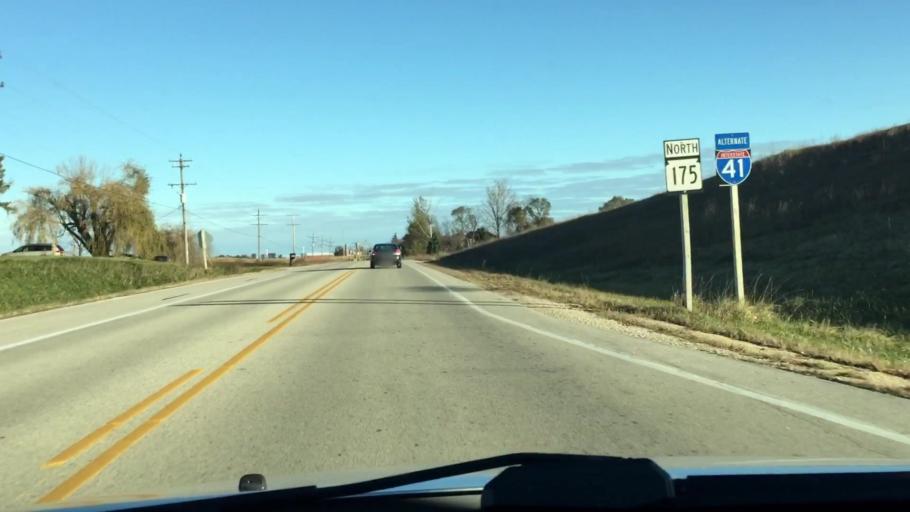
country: US
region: Wisconsin
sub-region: Dodge County
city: Lomira
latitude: 43.6020
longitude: -88.4503
